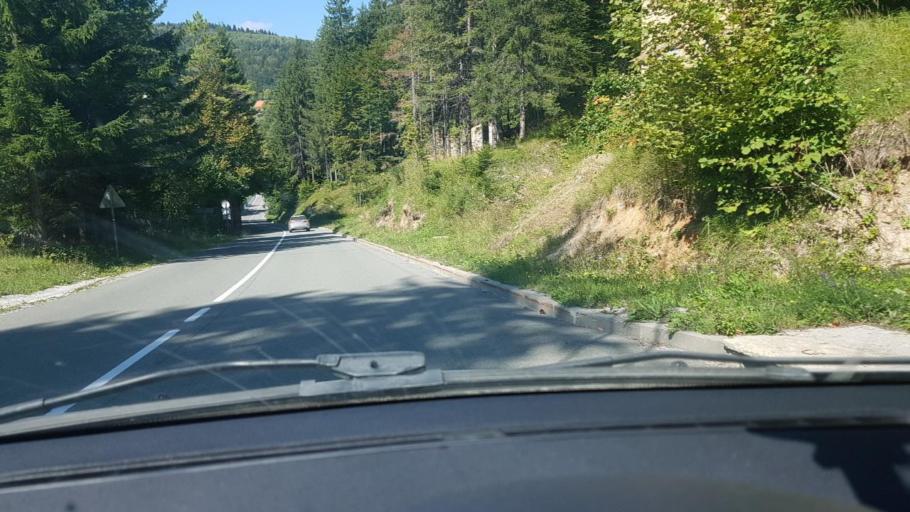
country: HR
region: Primorsko-Goranska
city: Vrbovsko
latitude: 45.3779
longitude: 14.9829
